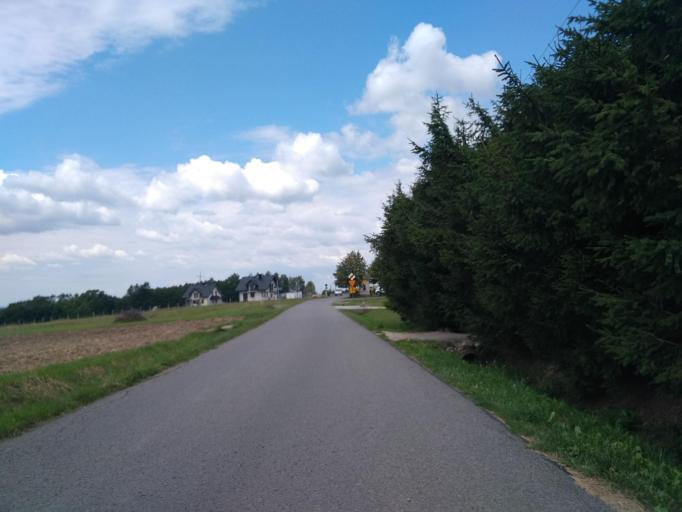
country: PL
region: Subcarpathian Voivodeship
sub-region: Powiat rzeszowski
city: Hyzne
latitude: 49.9168
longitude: 22.2126
